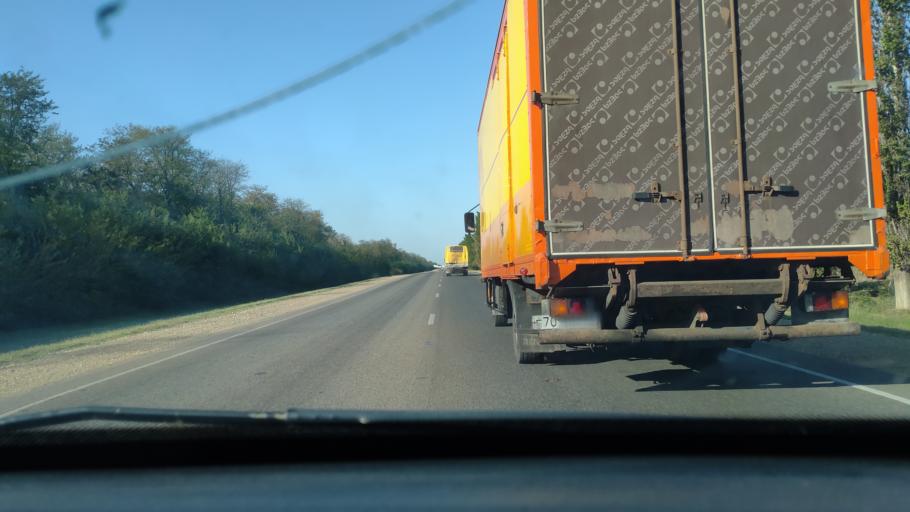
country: RU
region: Krasnodarskiy
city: Novotitarovskaya
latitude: 45.2641
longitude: 39.0011
